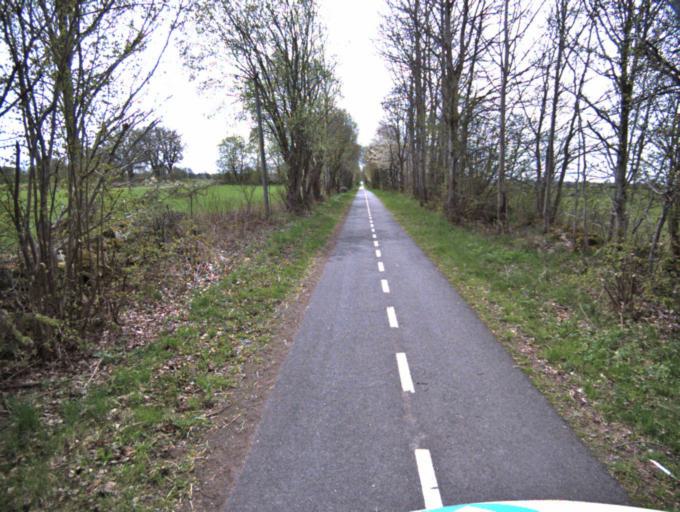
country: SE
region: Skane
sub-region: Kristianstads Kommun
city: Onnestad
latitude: 55.9871
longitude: 14.0297
